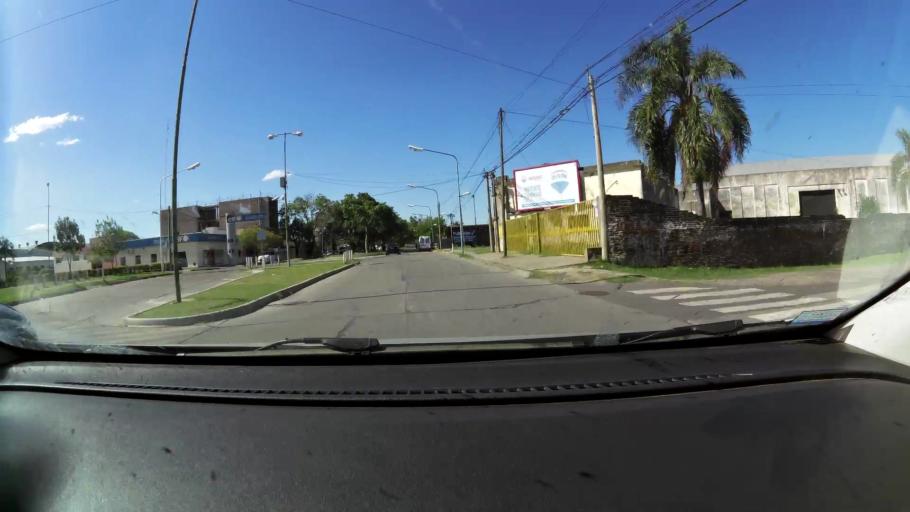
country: AR
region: Santa Fe
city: Rafaela
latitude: -31.2633
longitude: -61.4941
